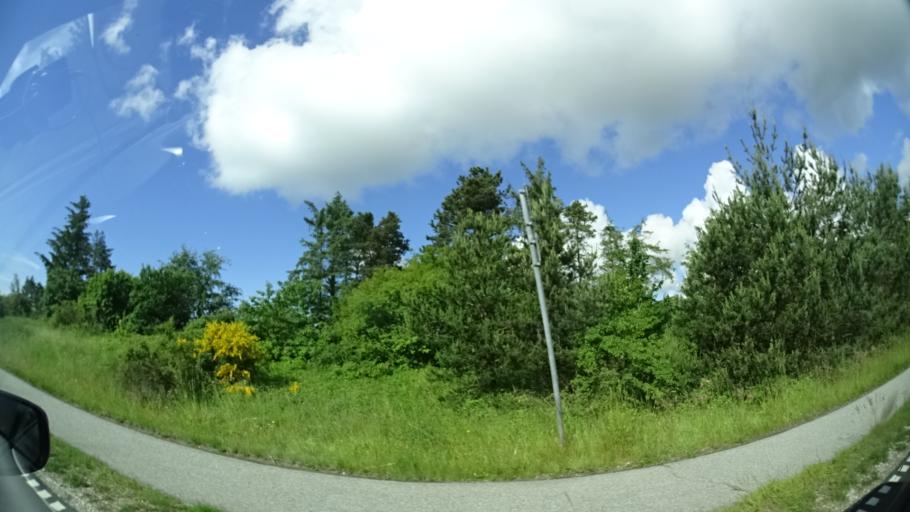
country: DK
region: Central Jutland
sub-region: Syddjurs Kommune
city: Ebeltoft
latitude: 56.2275
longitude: 10.6614
